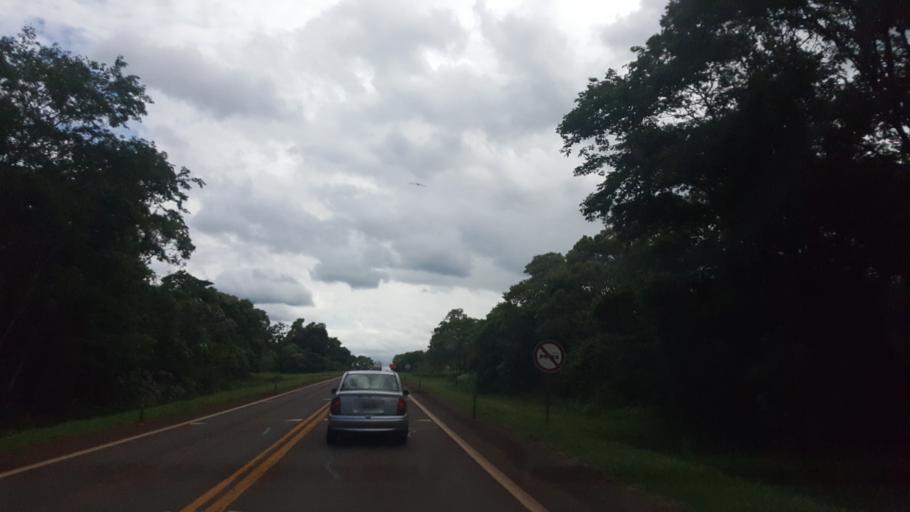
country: AR
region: Misiones
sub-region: Departamento de Iguazu
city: Puerto Iguazu
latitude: -25.7342
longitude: -54.5336
